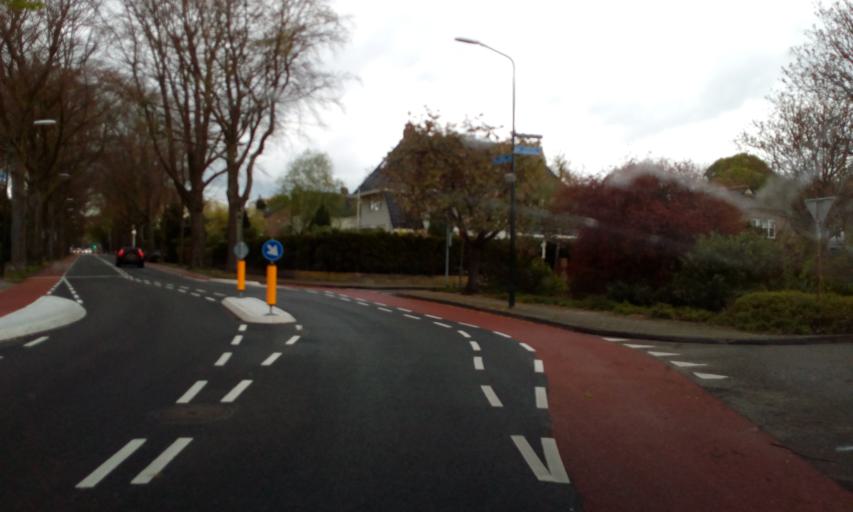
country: NL
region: North Holland
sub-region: Gemeente Huizen
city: Huizen
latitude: 52.2949
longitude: 5.2302
